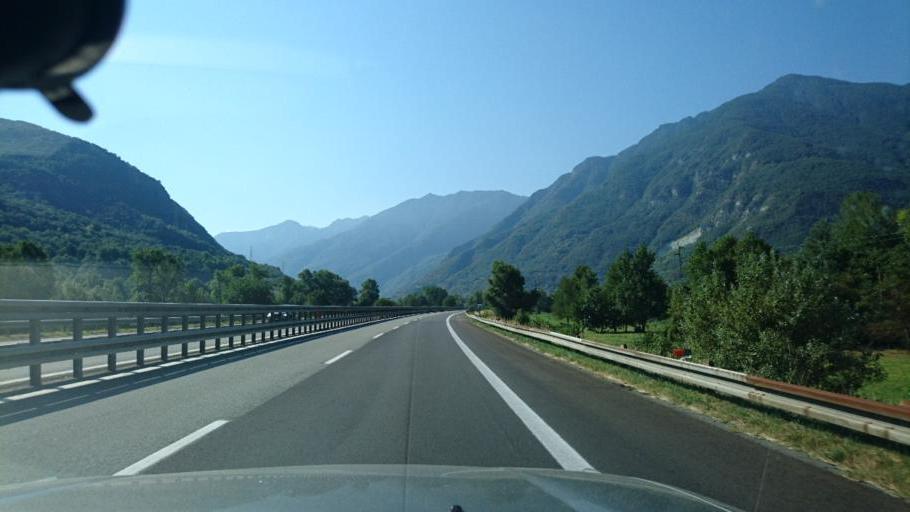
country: IT
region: Aosta Valley
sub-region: Valle d'Aosta
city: Montjovet
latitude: 45.6960
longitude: 7.6686
